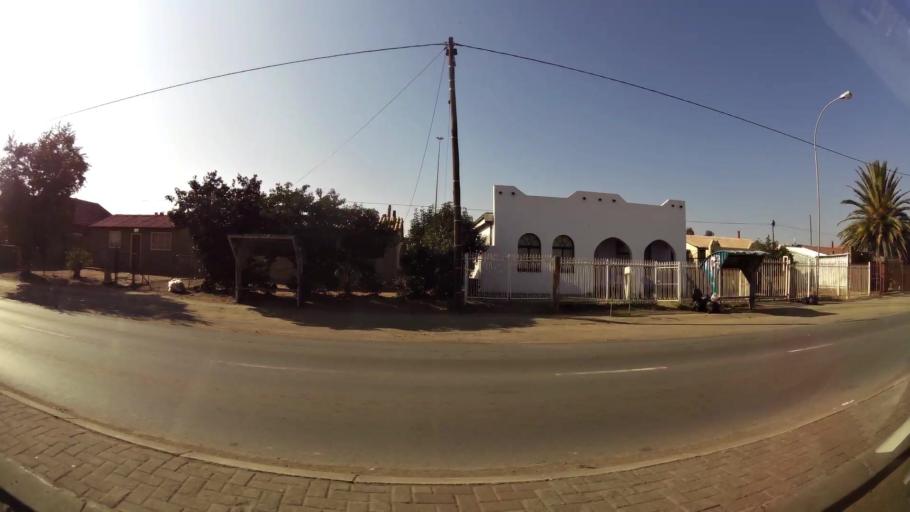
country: ZA
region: Orange Free State
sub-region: Mangaung Metropolitan Municipality
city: Bloemfontein
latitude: -29.1661
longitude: 26.2369
